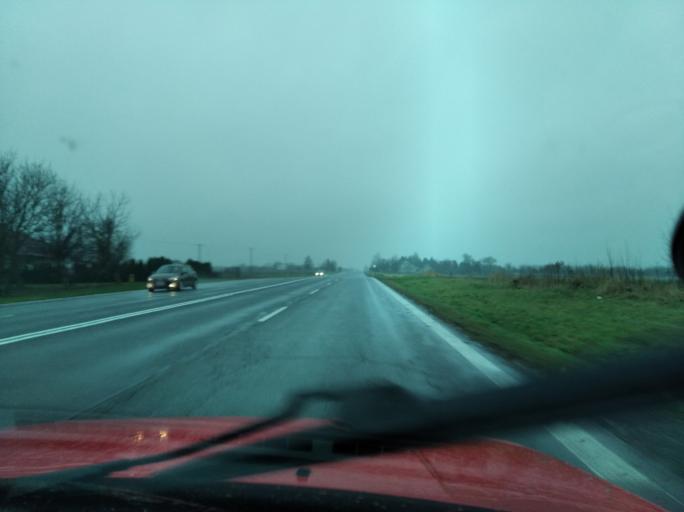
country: PL
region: Subcarpathian Voivodeship
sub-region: Powiat przeworski
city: Nowosielce
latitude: 50.0661
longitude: 22.4027
